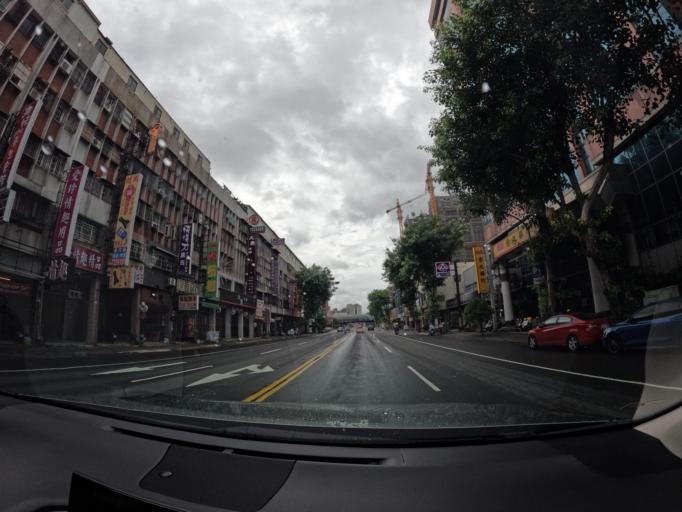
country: TW
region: Kaohsiung
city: Kaohsiung
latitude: 22.6312
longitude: 120.3340
